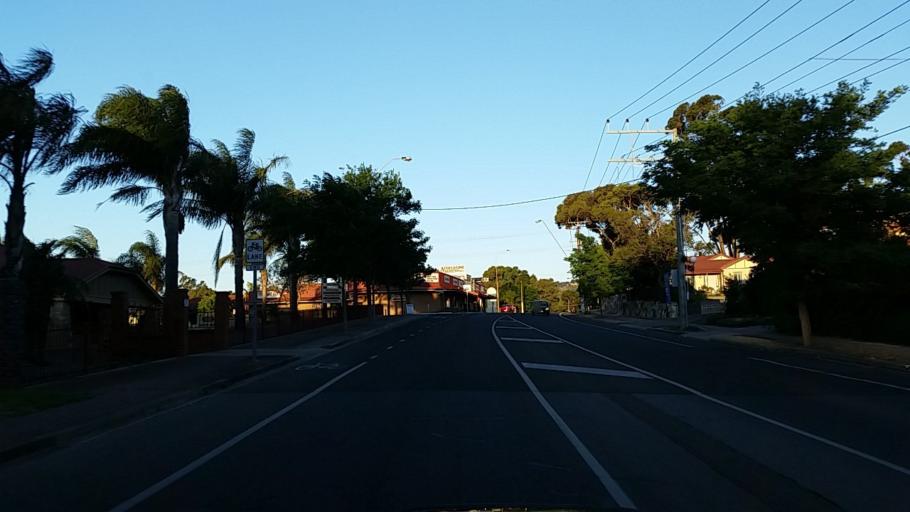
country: AU
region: South Australia
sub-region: Campbelltown
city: Athelstone
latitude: -34.8702
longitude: 138.7021
